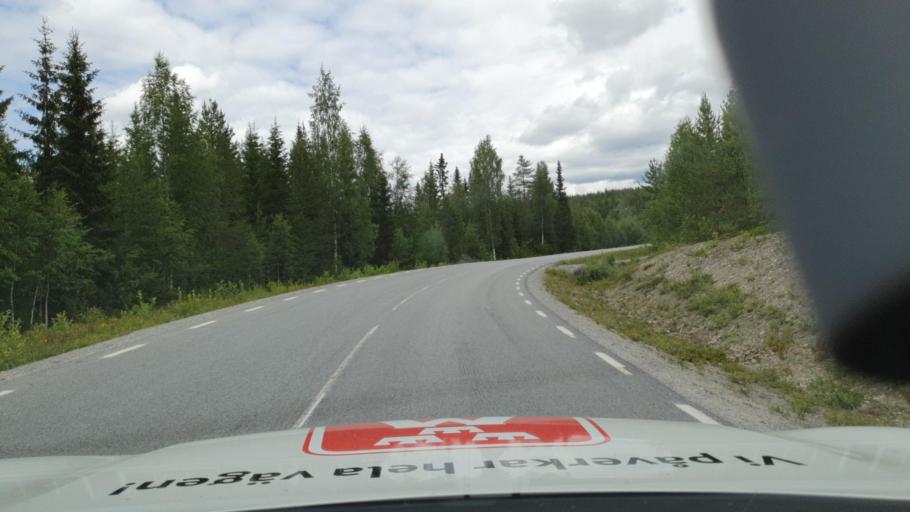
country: SE
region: Vaesterbotten
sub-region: Bjurholms Kommun
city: Bjurholm
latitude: 63.8820
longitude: 19.0203
